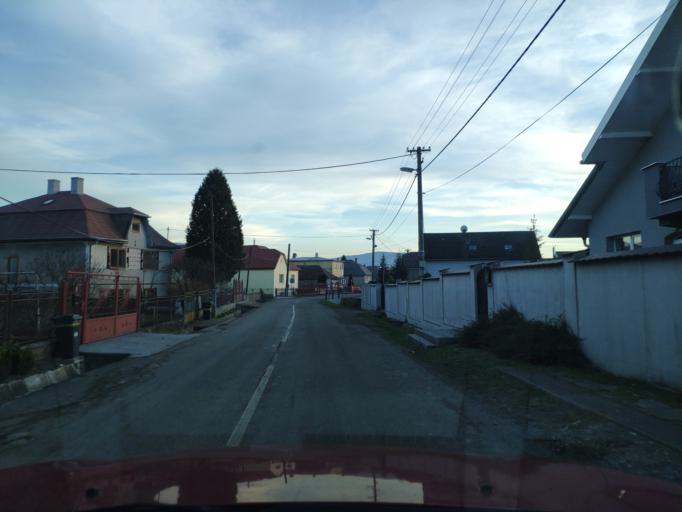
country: SK
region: Kosicky
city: Kosice
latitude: 48.7043
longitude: 21.4125
